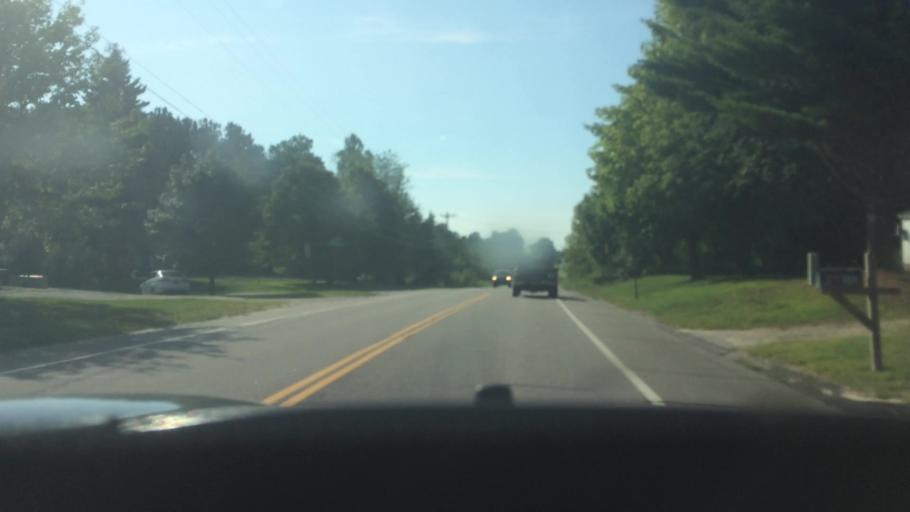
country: US
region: New York
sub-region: Franklin County
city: Malone
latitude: 44.8556
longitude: -74.2239
